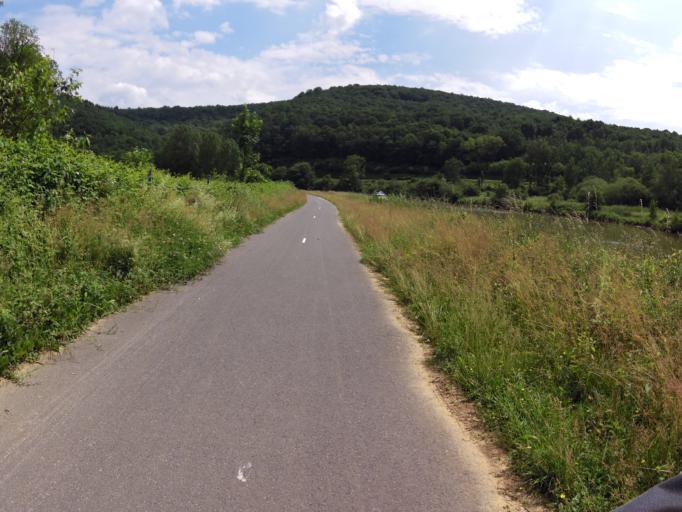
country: FR
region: Champagne-Ardenne
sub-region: Departement des Ardennes
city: Nouzonville
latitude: 49.8341
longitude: 4.7708
